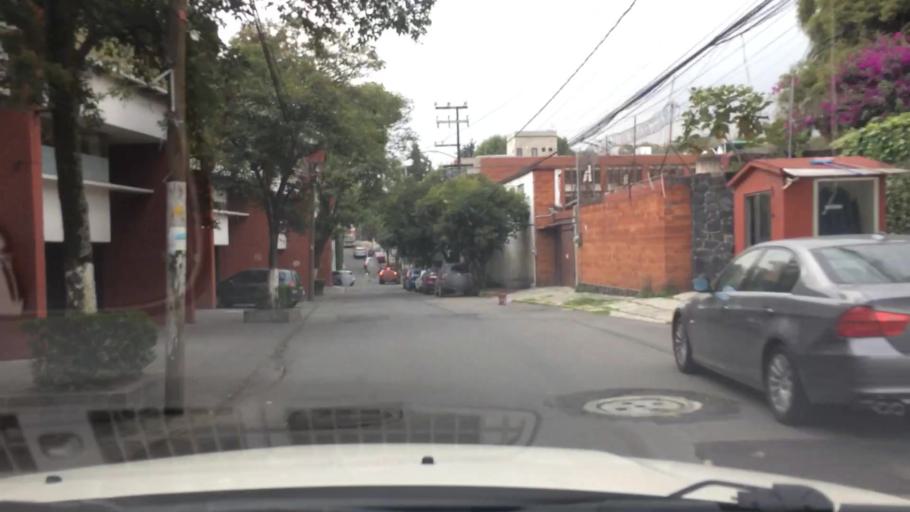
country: MX
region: Mexico City
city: Alvaro Obregon
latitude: 19.3545
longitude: -99.2011
